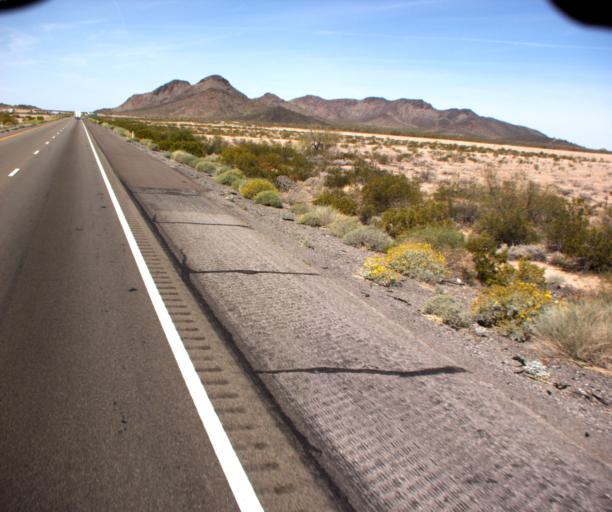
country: US
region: Arizona
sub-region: La Paz County
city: Salome
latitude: 33.6074
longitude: -113.6068
